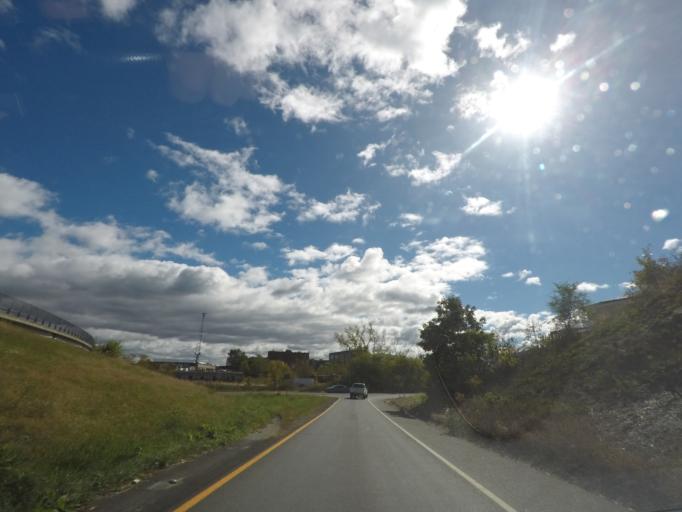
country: US
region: New York
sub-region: Albany County
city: Watervliet
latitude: 42.7204
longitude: -73.7169
